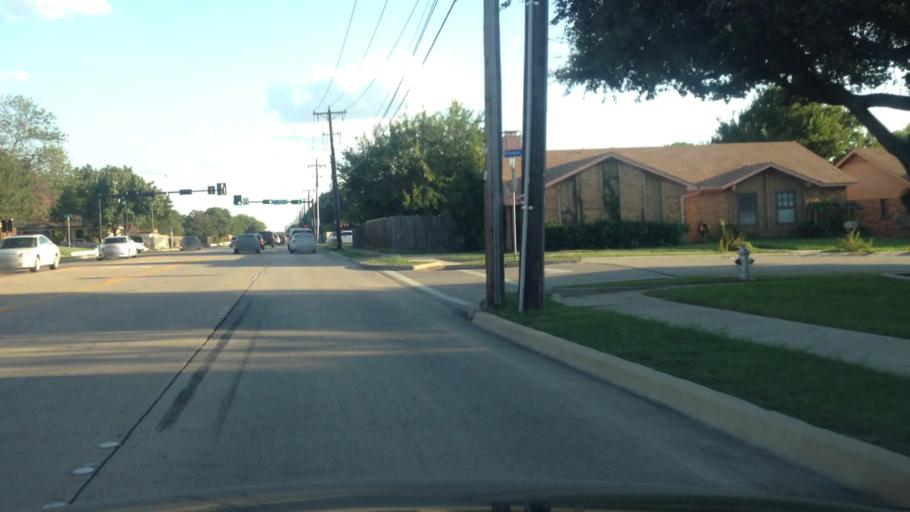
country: US
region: Texas
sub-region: Tarrant County
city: Watauga
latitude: 32.8824
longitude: -97.2379
